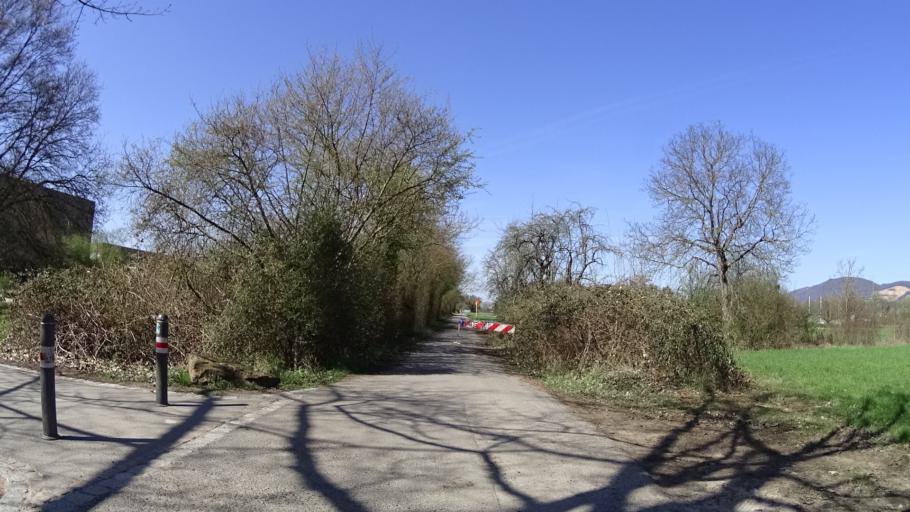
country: DE
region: Baden-Wuerttemberg
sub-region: Karlsruhe Region
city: Dossenheim
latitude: 49.4232
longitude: 8.6624
